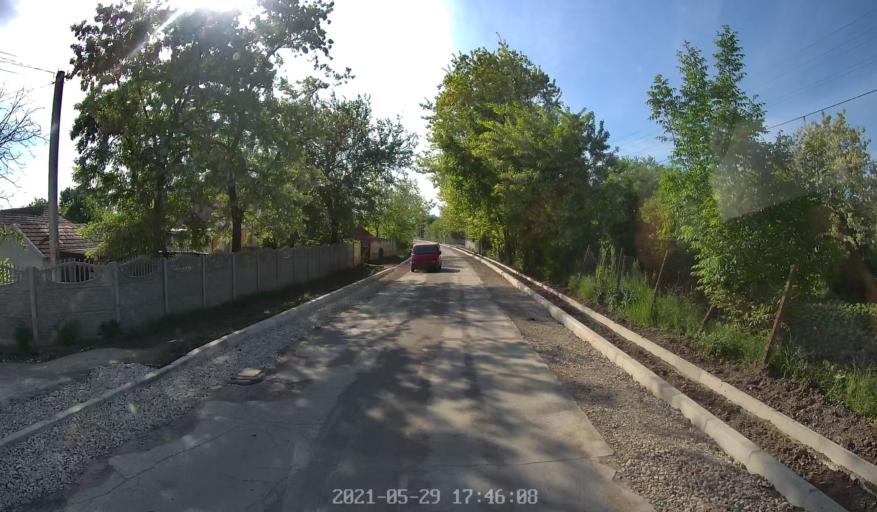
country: MD
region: Laloveni
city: Ialoveni
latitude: 46.8387
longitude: 28.8416
